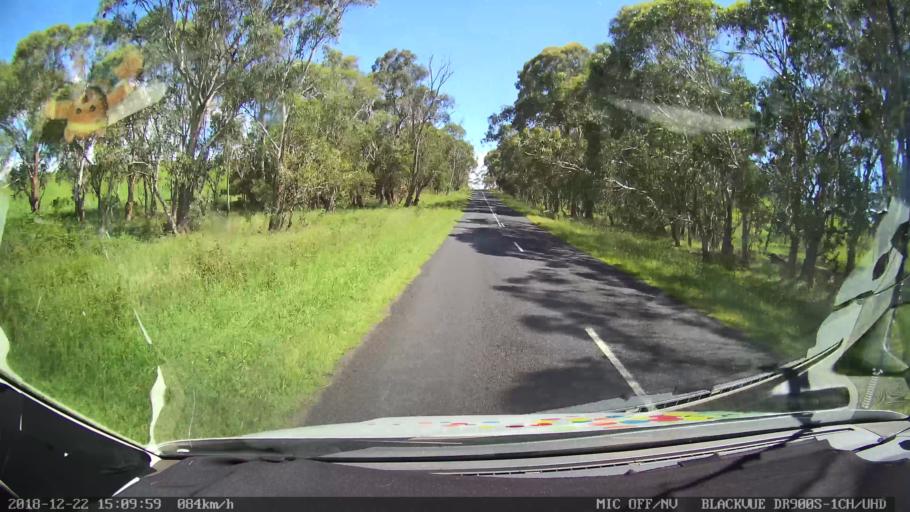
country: AU
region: New South Wales
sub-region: Bellingen
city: Dorrigo
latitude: -30.3298
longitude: 152.4057
